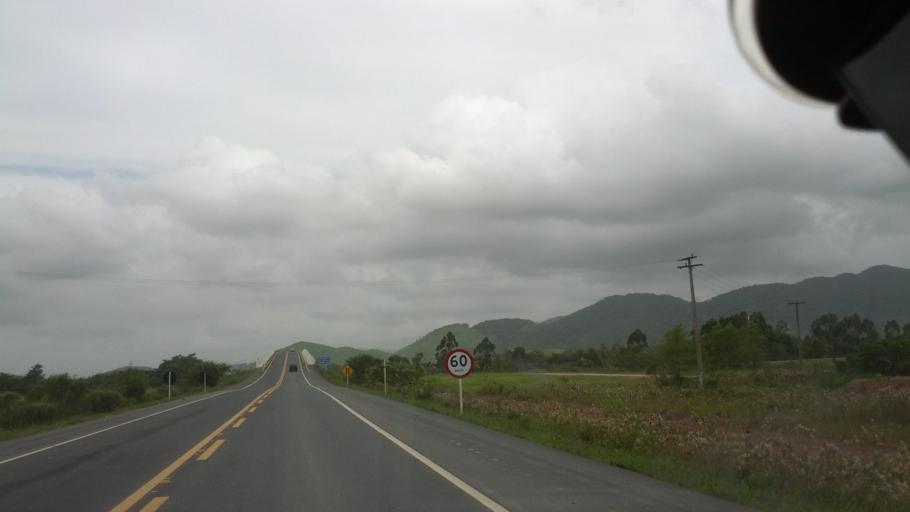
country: BR
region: Santa Catarina
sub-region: Gaspar
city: Gaspar
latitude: -26.8913
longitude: -48.8281
